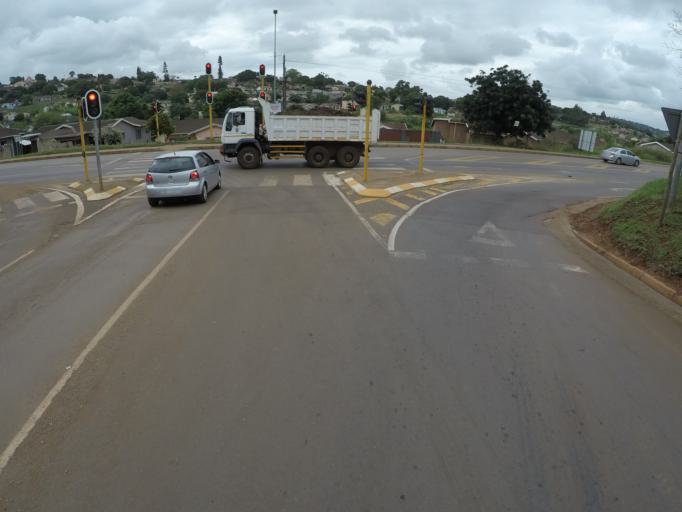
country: ZA
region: KwaZulu-Natal
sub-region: uThungulu District Municipality
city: Empangeni
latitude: -28.7740
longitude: 31.8656
